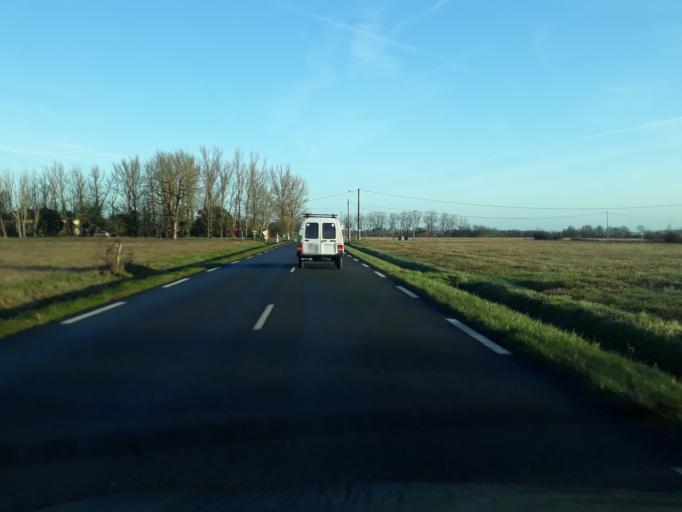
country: FR
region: Midi-Pyrenees
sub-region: Departement de la Haute-Garonne
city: Rieumes
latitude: 43.4424
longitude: 1.1359
